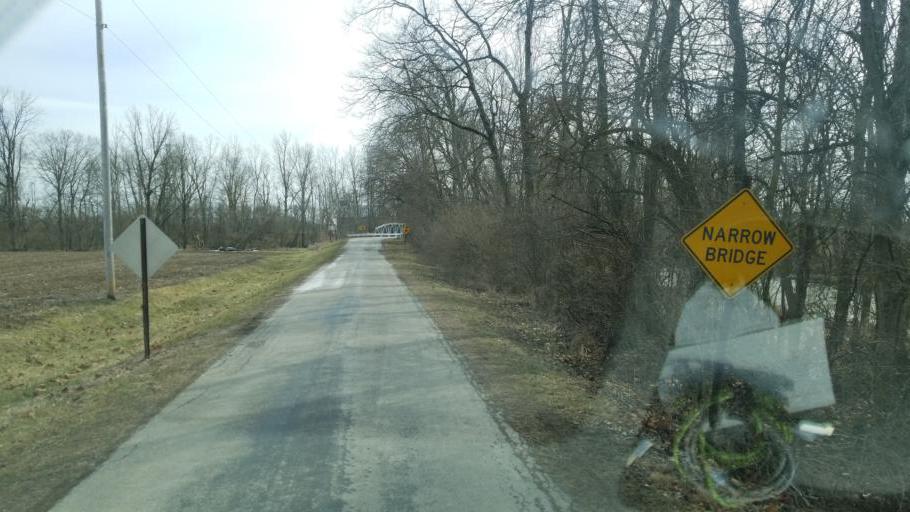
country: US
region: Ohio
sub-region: Marion County
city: Prospect
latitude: 40.3363
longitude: -83.2129
